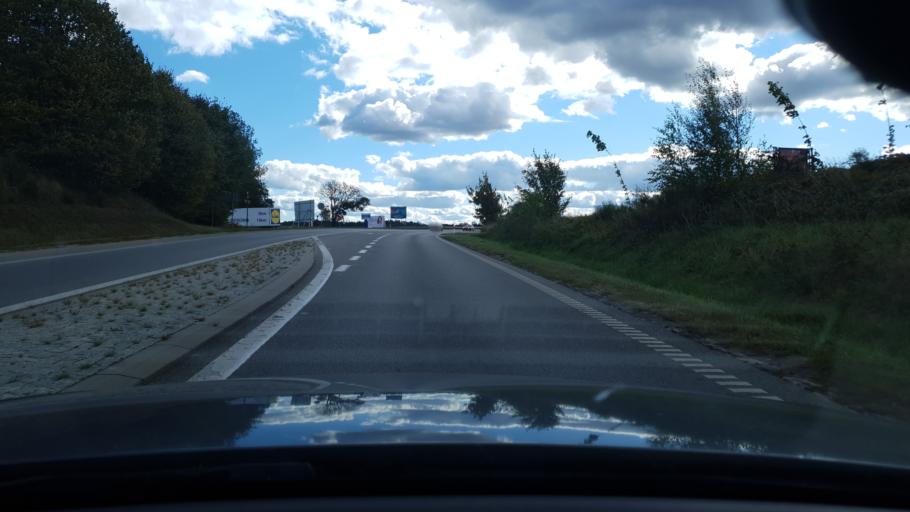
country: PL
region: Pomeranian Voivodeship
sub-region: Powiat wejherowski
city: Rekowo Dolne
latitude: 54.6567
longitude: 18.3626
